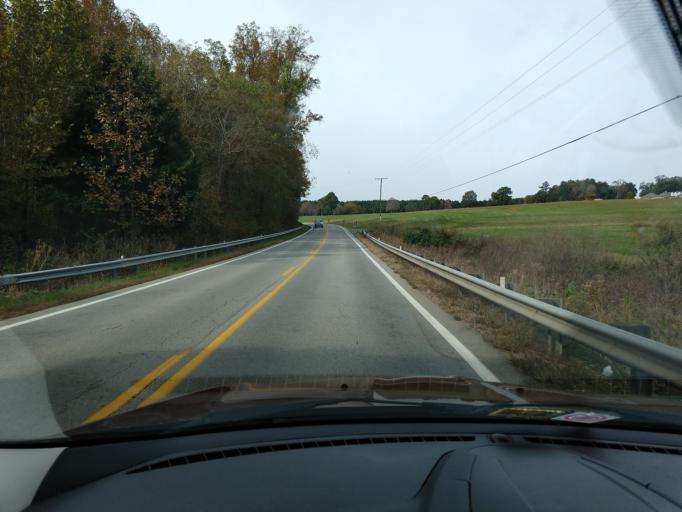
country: US
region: Virginia
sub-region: Pittsylvania County
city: Gretna
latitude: 36.9530
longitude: -79.4292
